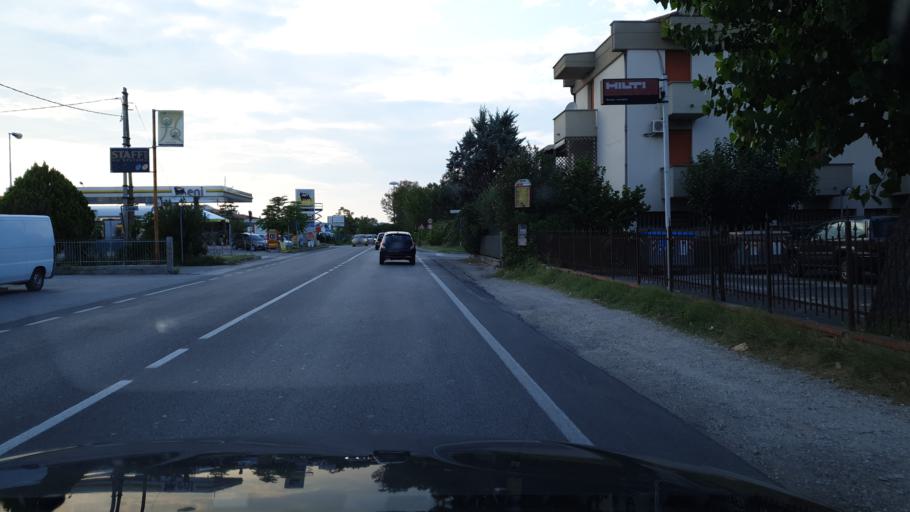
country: IT
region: Emilia-Romagna
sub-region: Provincia di Rimini
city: Rivazzurra
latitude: 44.0355
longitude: 12.6004
